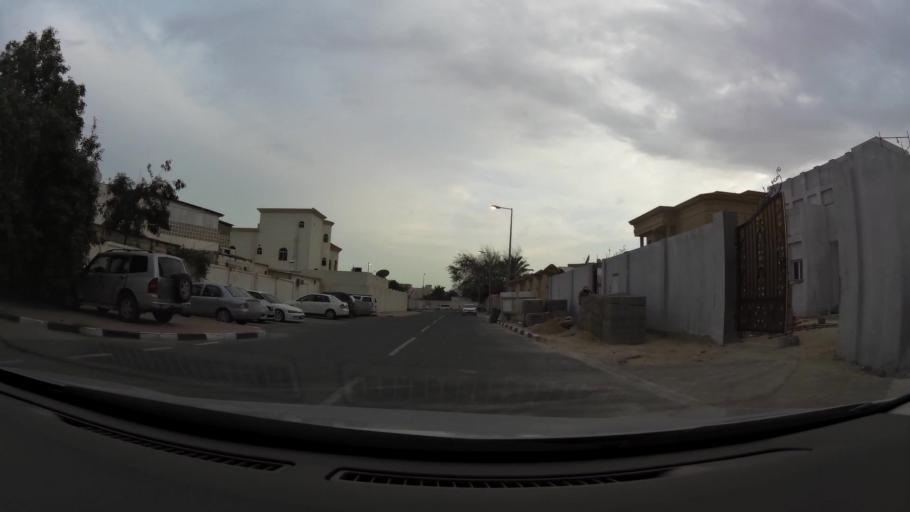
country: QA
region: Baladiyat ad Dawhah
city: Doha
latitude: 25.3418
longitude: 51.5083
